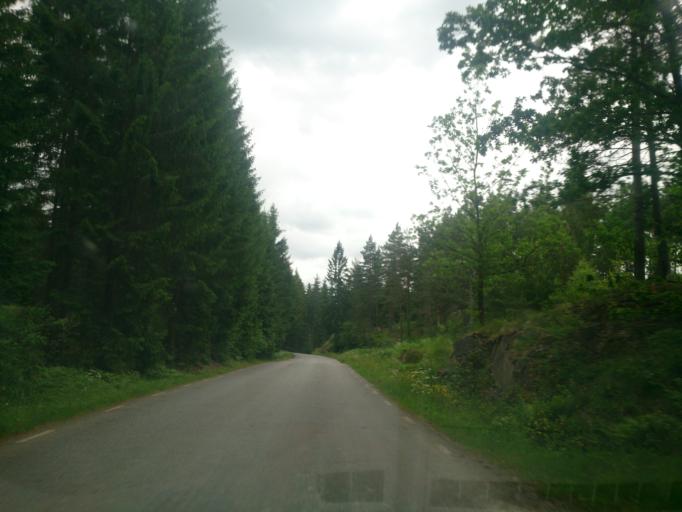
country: SE
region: OEstergoetland
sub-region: Soderkopings Kommun
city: Soederkoeping
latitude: 58.3146
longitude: 16.2863
